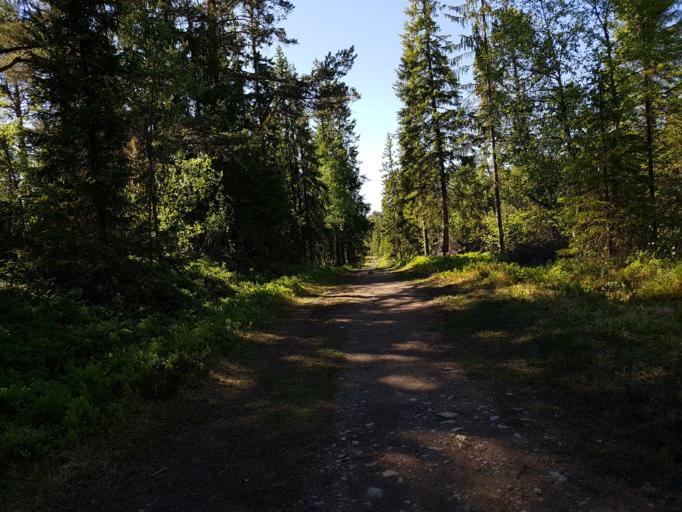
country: NO
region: Sor-Trondelag
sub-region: Trondheim
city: Trondheim
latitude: 63.4275
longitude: 10.2960
